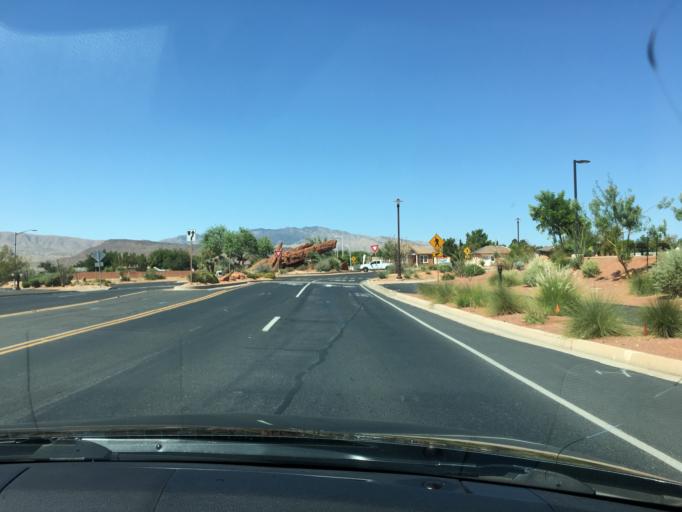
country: US
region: Utah
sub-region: Washington County
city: Ivins
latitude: 37.1685
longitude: -113.6740
